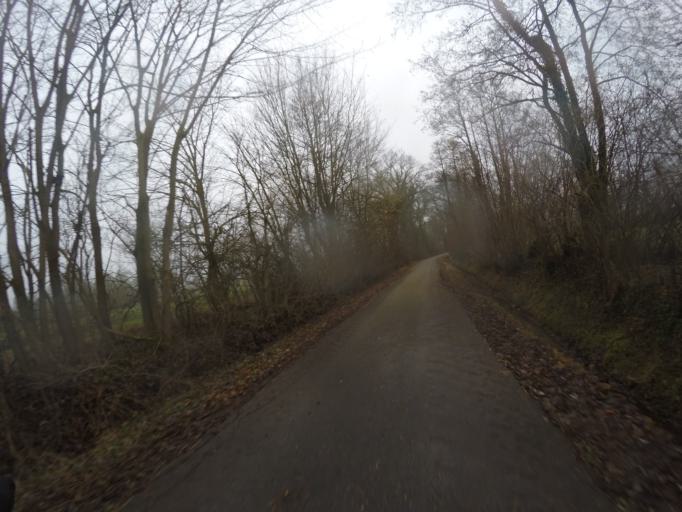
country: DE
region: Schleswig-Holstein
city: Ellerau
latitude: 53.7606
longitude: 9.9057
